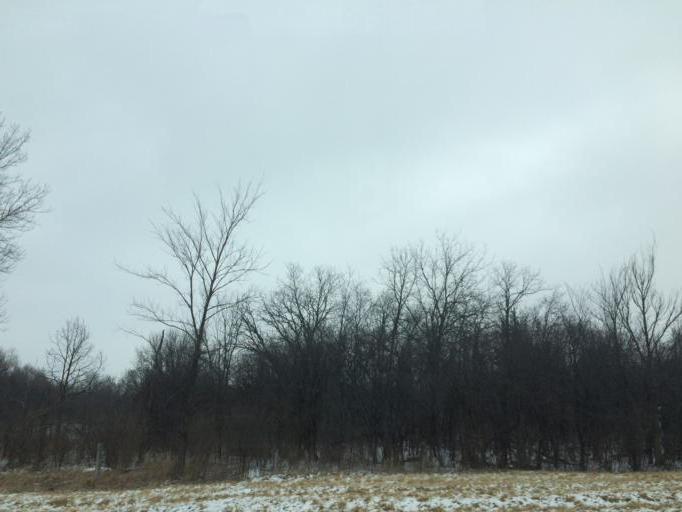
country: US
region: Illinois
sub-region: McHenry County
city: Lakewood
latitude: 42.2463
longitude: -88.4235
